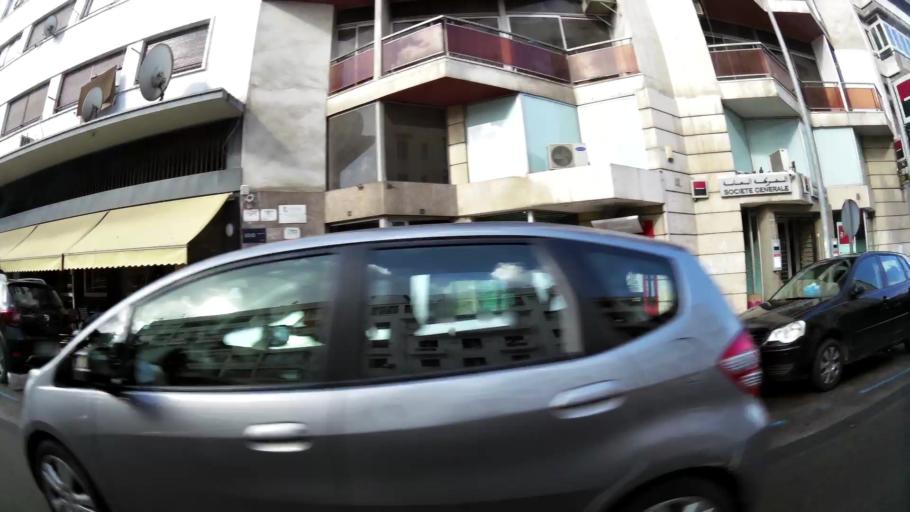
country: MA
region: Grand Casablanca
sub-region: Casablanca
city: Casablanca
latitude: 33.5876
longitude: -7.6122
